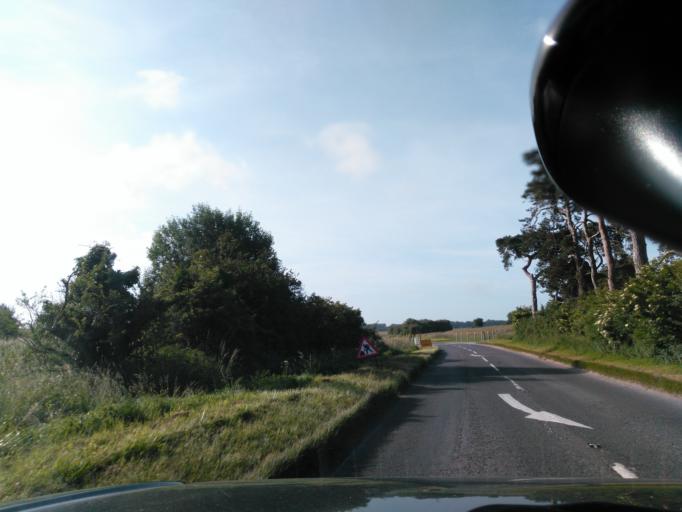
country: GB
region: England
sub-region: Wiltshire
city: Market Lavington
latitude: 51.2391
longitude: -1.9739
